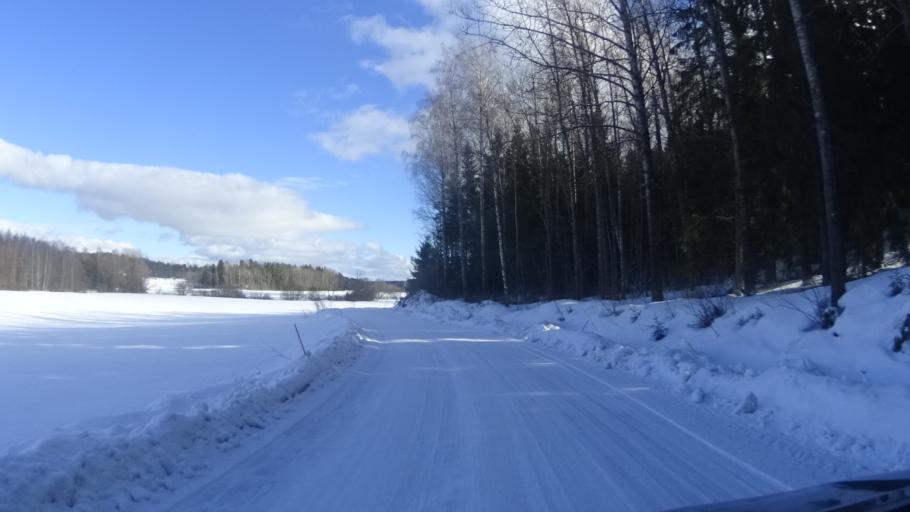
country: FI
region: Uusimaa
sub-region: Helsinki
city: Vantaa
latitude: 60.2482
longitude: 25.1672
